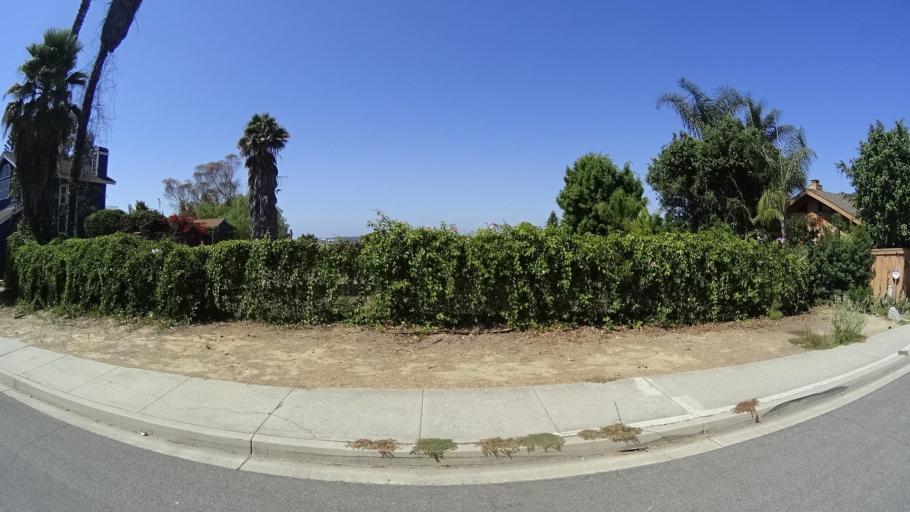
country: US
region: California
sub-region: San Diego County
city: Lake San Marcos
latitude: 33.1281
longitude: -117.2157
